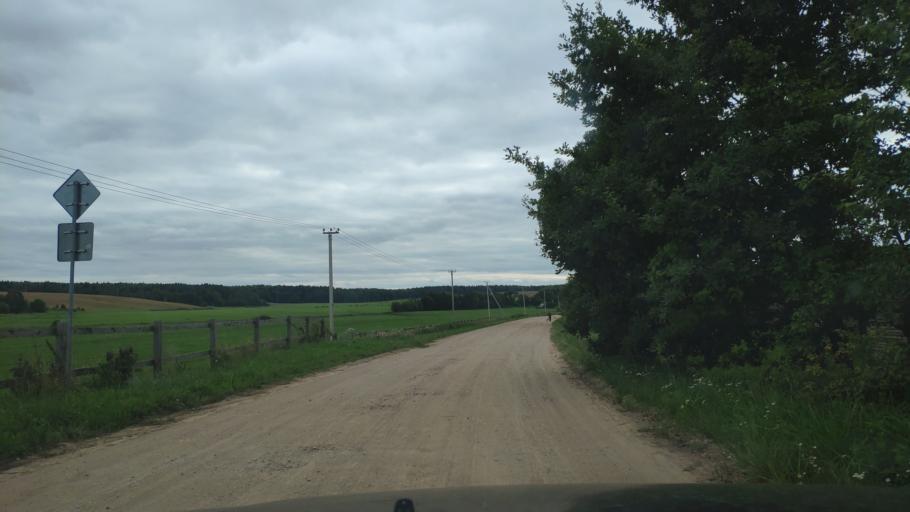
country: BY
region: Minsk
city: Khatsyezhyna
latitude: 53.9304
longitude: 27.2666
